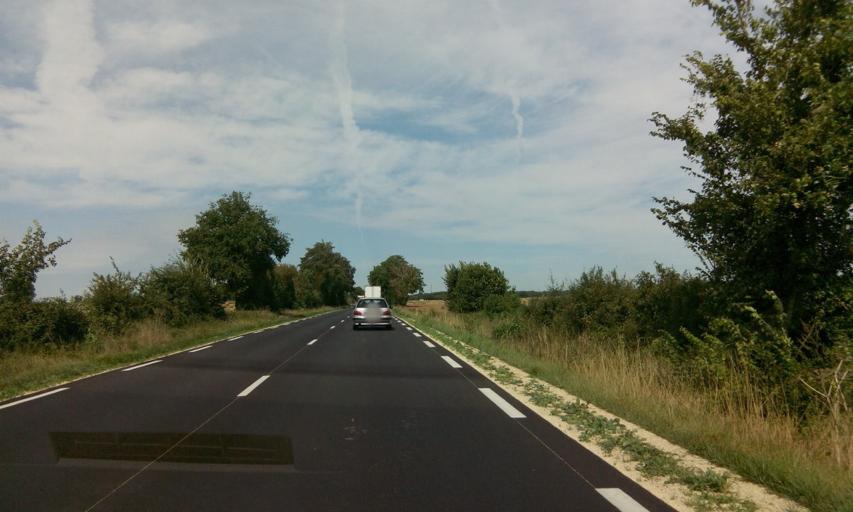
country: FR
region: Poitou-Charentes
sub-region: Departement des Deux-Sevres
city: Sauze-Vaussais
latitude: 46.1430
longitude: 0.0851
